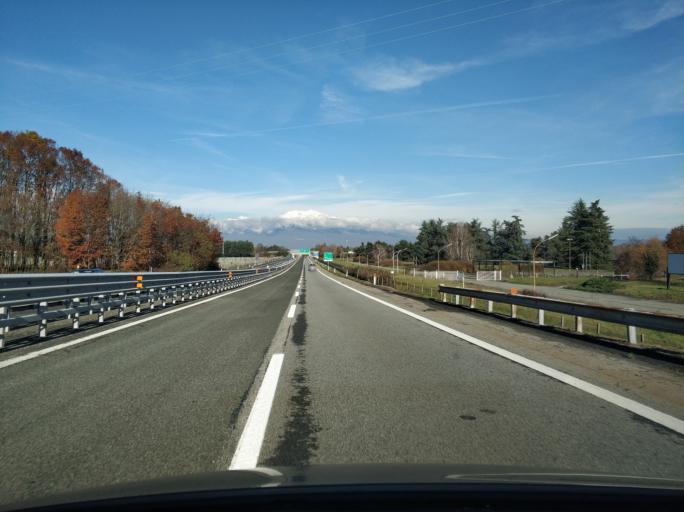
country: IT
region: Piedmont
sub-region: Provincia di Torino
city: Scarmagno
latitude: 45.3798
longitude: 7.8455
